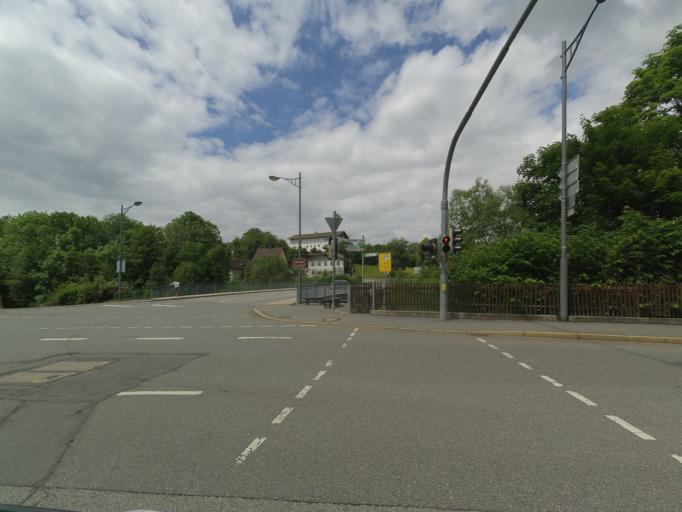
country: DE
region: Bavaria
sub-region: Lower Bavaria
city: Zwiesel
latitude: 49.0228
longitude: 13.2311
